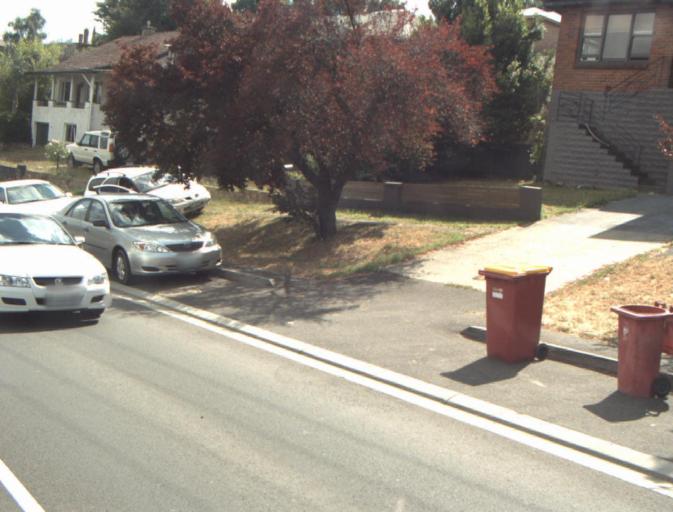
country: AU
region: Tasmania
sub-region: Launceston
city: West Launceston
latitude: -41.4620
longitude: 147.1461
